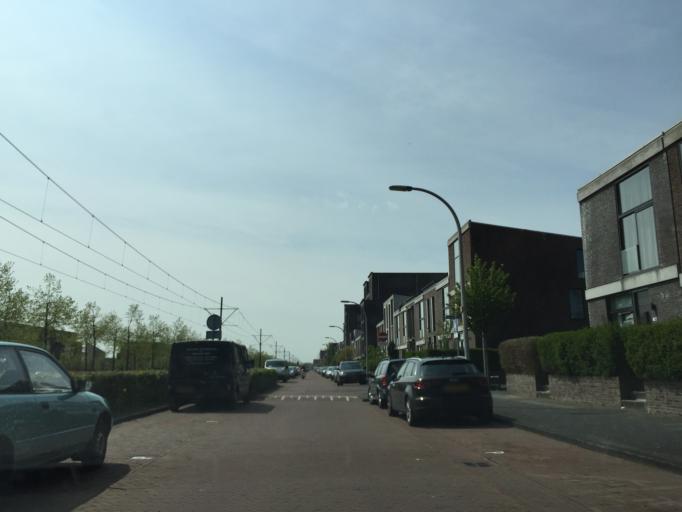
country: NL
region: South Holland
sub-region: Gemeente Den Haag
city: Ypenburg
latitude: 52.0471
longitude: 4.3803
